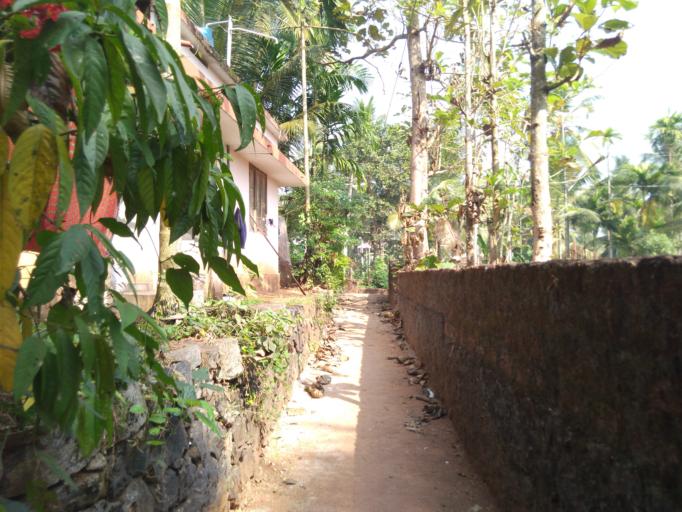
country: IN
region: Kerala
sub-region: Kozhikode
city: Kunnamangalam
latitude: 11.2899
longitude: 75.8306
